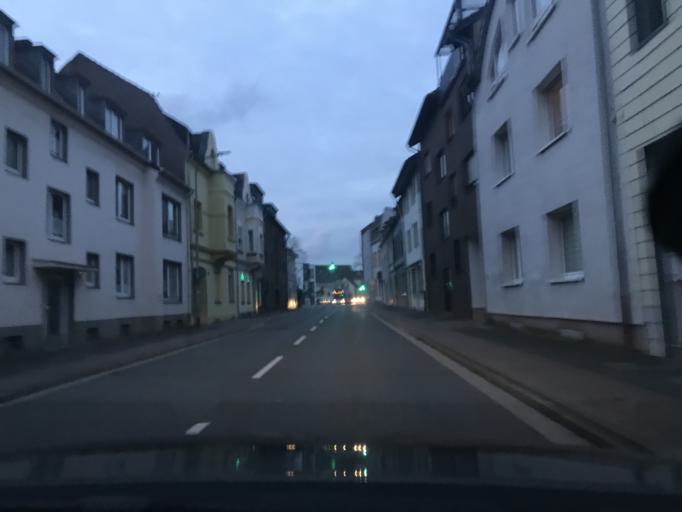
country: DE
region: North Rhine-Westphalia
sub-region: Regierungsbezirk Dusseldorf
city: Moers
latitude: 51.4452
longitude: 6.6274
